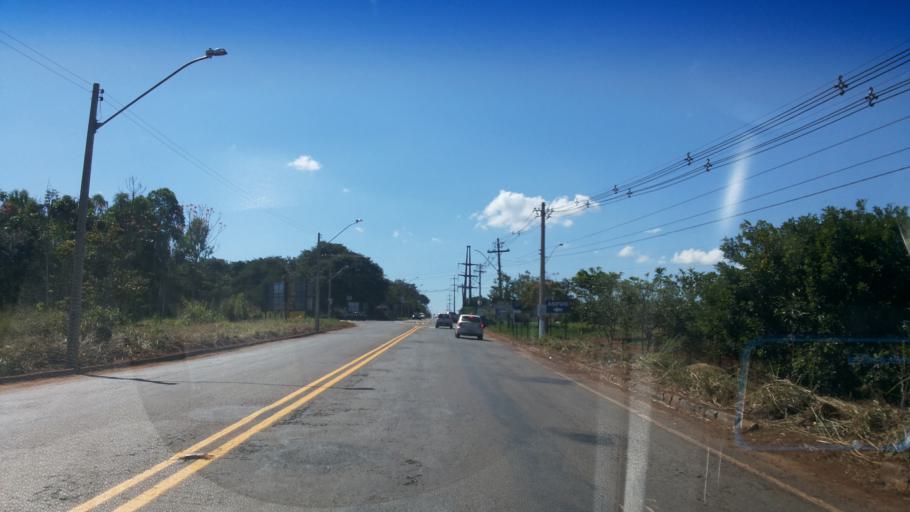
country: BR
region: Goias
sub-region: Goiania
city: Goiania
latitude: -16.6043
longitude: -49.2812
